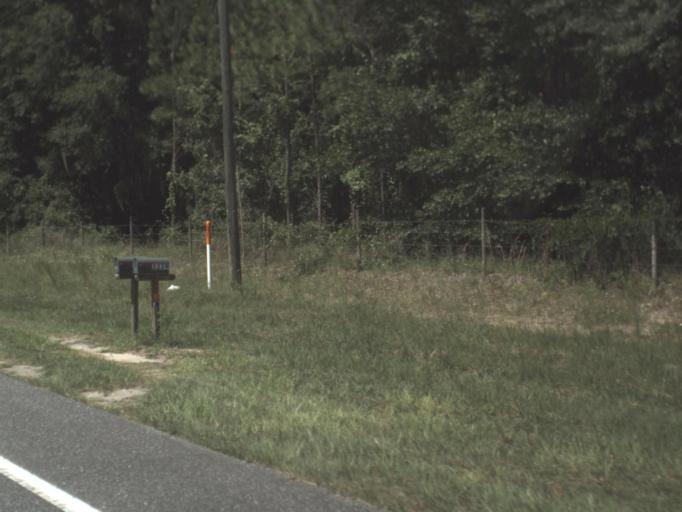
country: US
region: Florida
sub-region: Alachua County
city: High Springs
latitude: 29.7859
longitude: -82.7409
